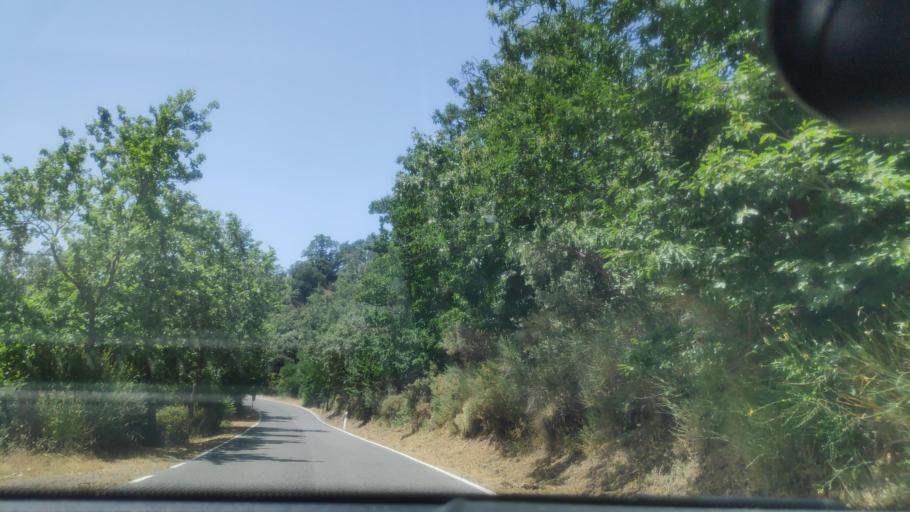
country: ES
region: Andalusia
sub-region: Provincia de Granada
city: Trevelez
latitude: 36.9780
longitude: -3.2781
